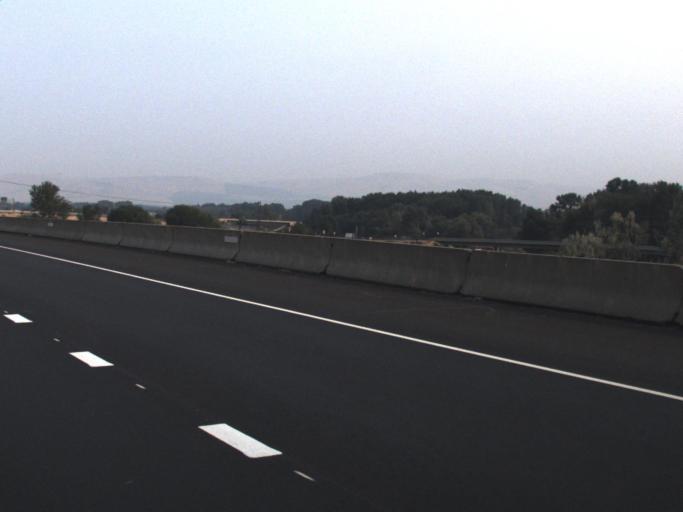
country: US
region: Washington
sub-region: Yakima County
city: Union Gap
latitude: 46.5342
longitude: -120.4740
